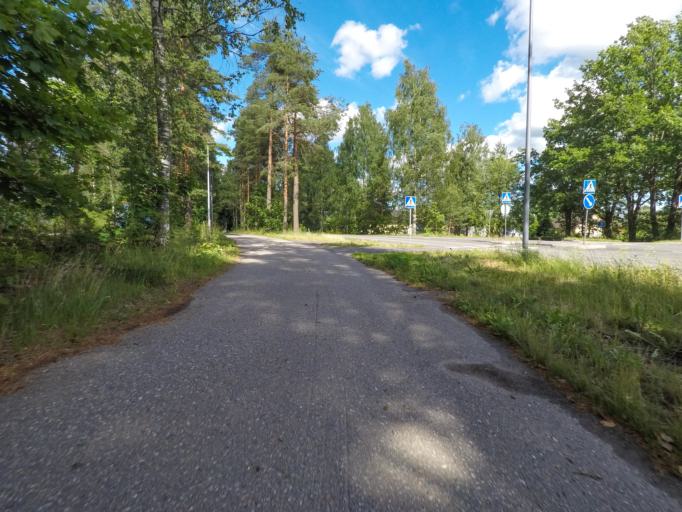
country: FI
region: South Karelia
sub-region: Lappeenranta
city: Lappeenranta
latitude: 61.0796
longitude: 28.3259
